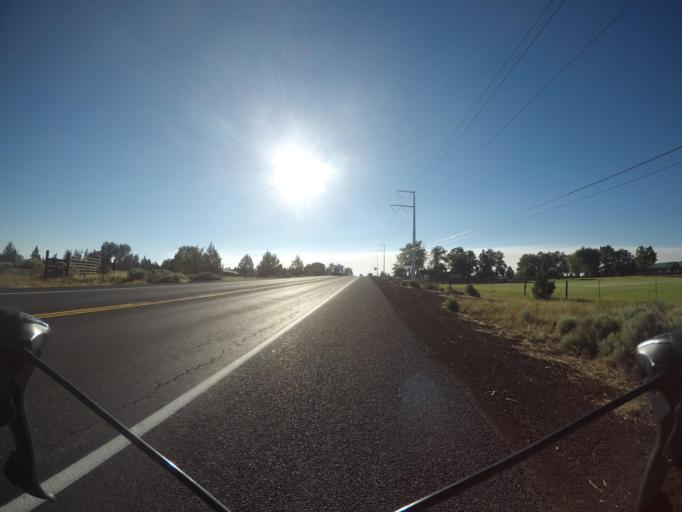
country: US
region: Oregon
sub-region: Deschutes County
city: Redmond
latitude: 44.2730
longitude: -121.2536
